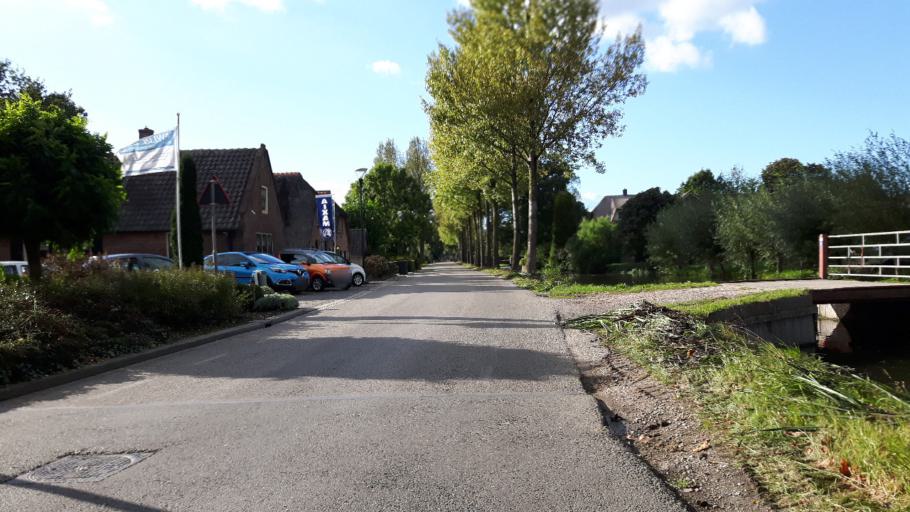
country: NL
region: Utrecht
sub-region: Gemeente Vianen
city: Vianen
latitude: 51.9460
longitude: 5.0748
